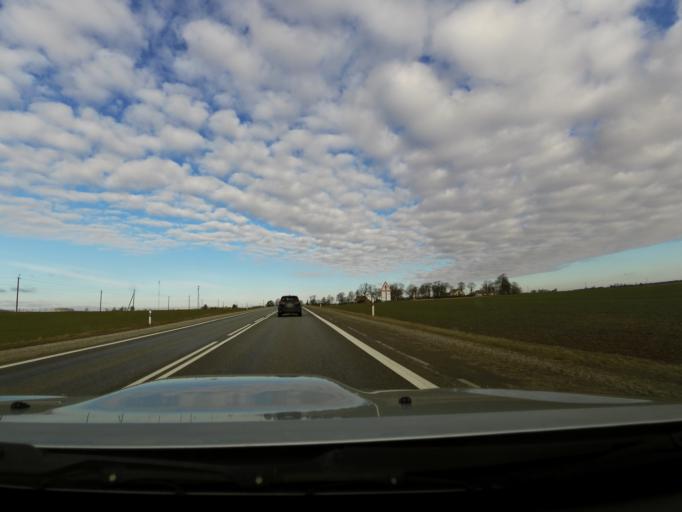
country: LT
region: Siauliu apskritis
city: Pakruojis
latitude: 55.7857
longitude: 24.0387
